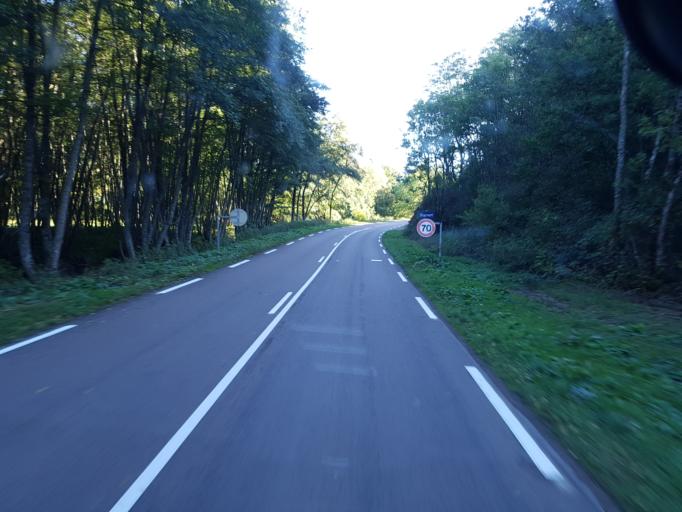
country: FR
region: Bourgogne
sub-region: Departement de Saone-et-Loire
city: Autun
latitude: 47.1043
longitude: 4.2304
